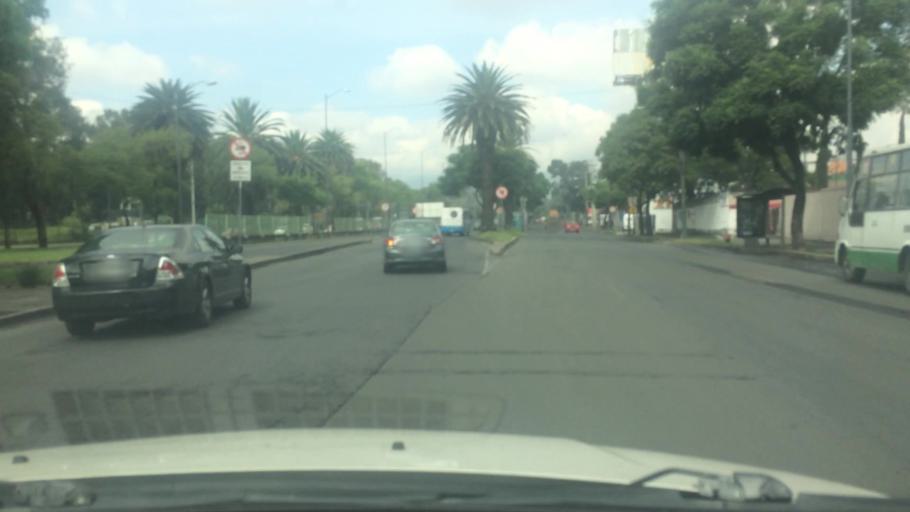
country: MX
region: Mexico City
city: Xochimilco
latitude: 19.2942
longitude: -99.1041
